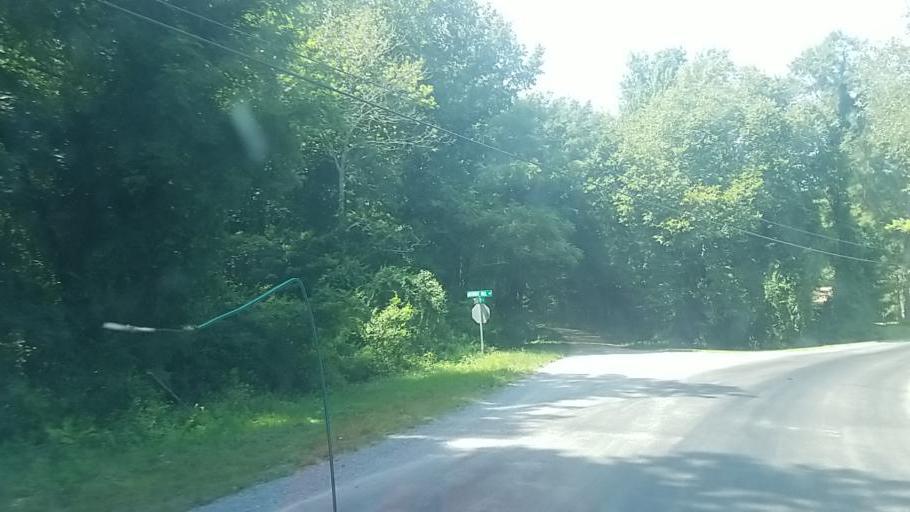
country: US
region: Maryland
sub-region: Caroline County
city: Denton
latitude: 38.8780
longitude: -75.7883
